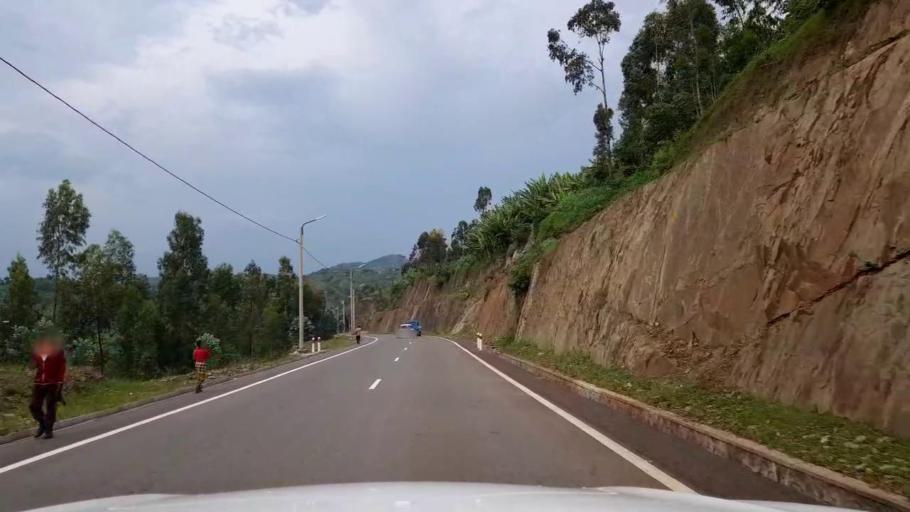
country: RW
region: Western Province
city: Kibuye
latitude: -2.0377
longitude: 29.4010
